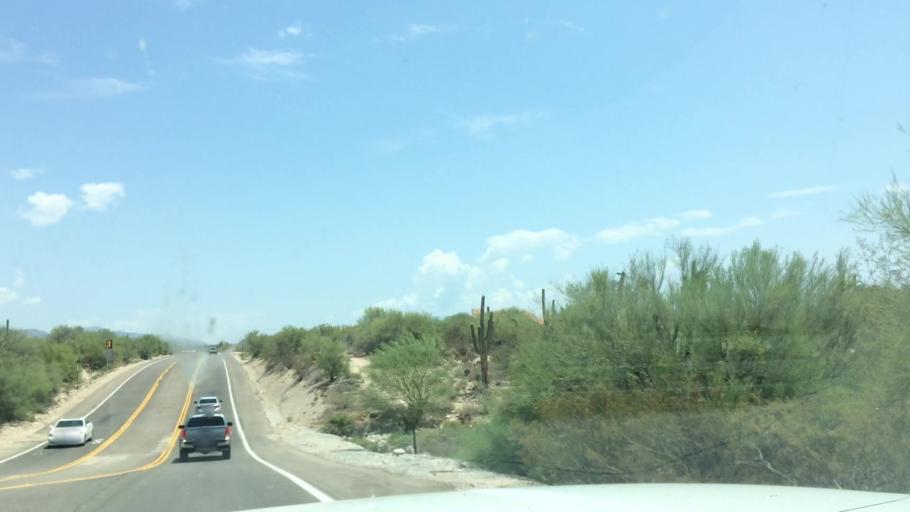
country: US
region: Arizona
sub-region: Pima County
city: Casas Adobes
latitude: 32.3228
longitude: -110.9586
